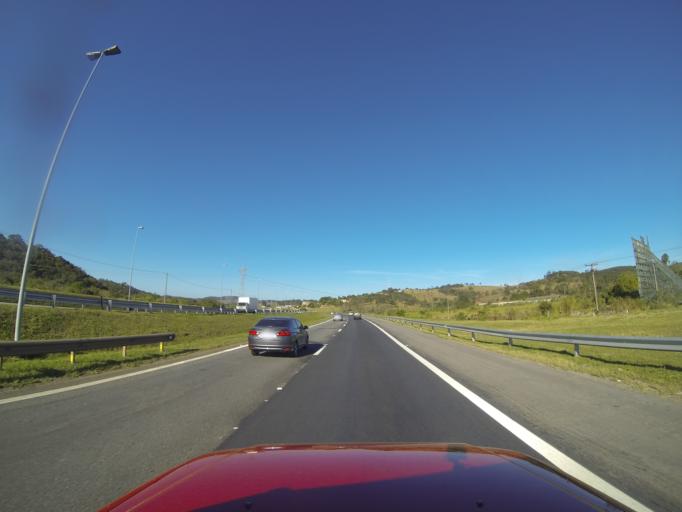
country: BR
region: Sao Paulo
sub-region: Bom Jesus Dos Perdoes
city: Bom Jesus dos Perdoes
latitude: -23.1714
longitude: -46.4265
